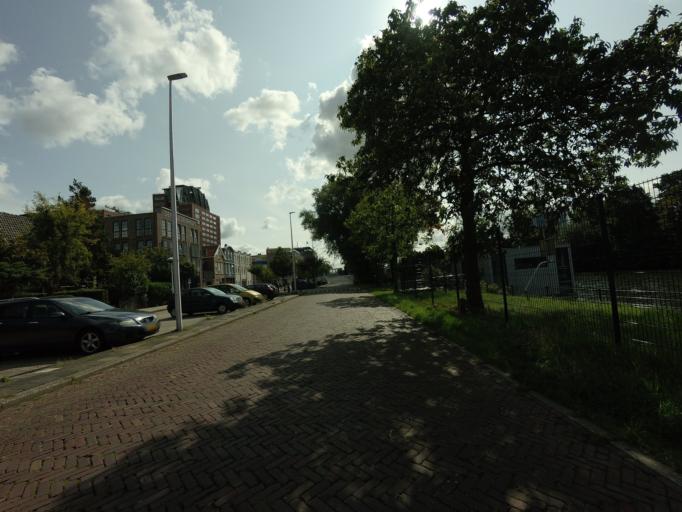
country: NL
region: Utrecht
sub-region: Gemeente Utrecht
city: Utrecht
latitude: 52.0864
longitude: 5.0970
